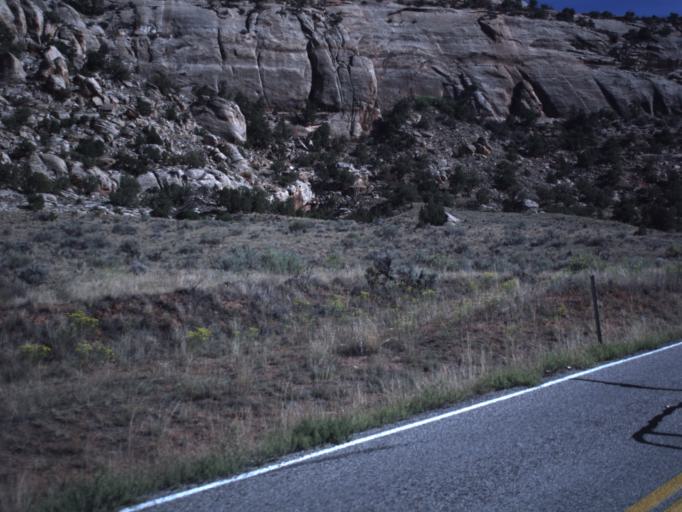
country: US
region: Utah
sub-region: San Juan County
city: Monticello
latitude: 38.0199
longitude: -109.5388
